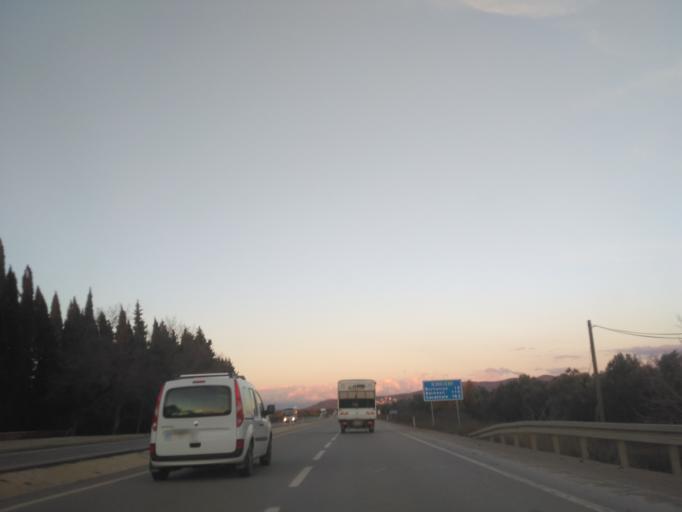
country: TR
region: Balikesir
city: Emrutabat
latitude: 39.3973
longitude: 26.8440
